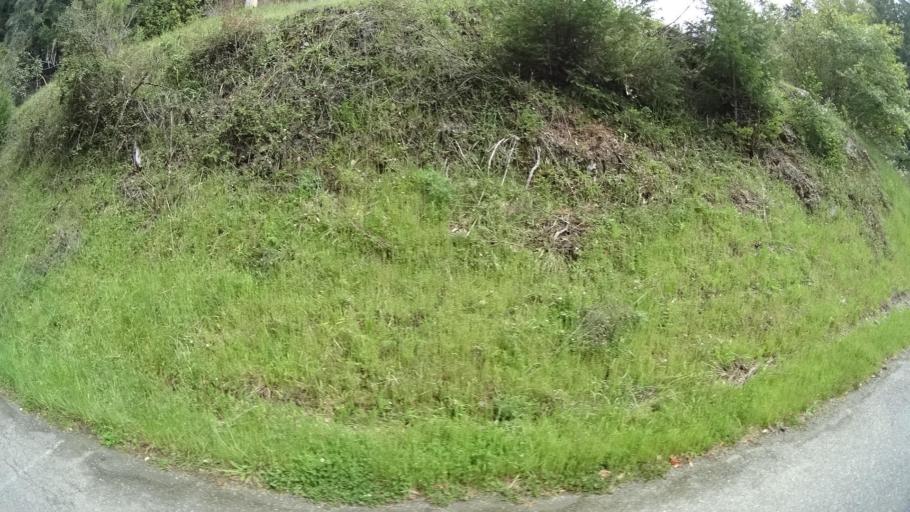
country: US
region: California
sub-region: Humboldt County
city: Blue Lake
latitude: 40.7939
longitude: -123.9776
